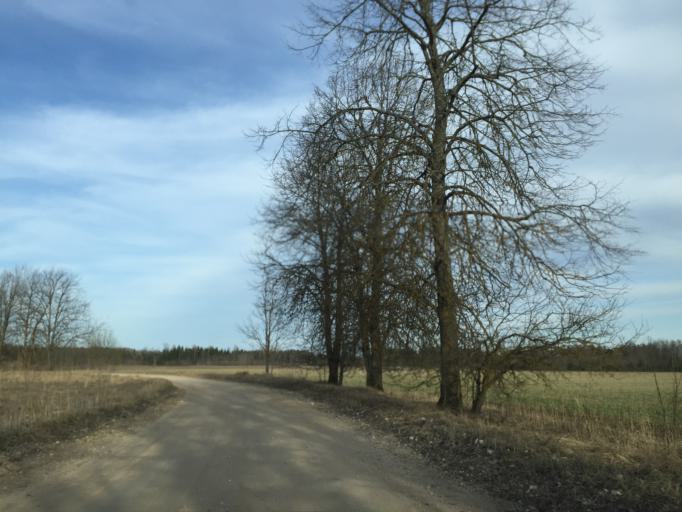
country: LV
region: Kegums
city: Kegums
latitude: 56.7957
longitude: 24.7603
